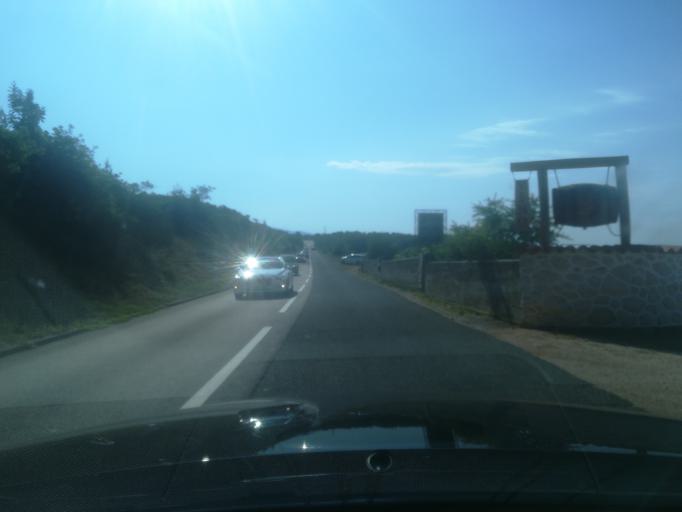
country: HR
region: Primorsko-Goranska
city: Banjol
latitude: 44.7087
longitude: 14.8334
